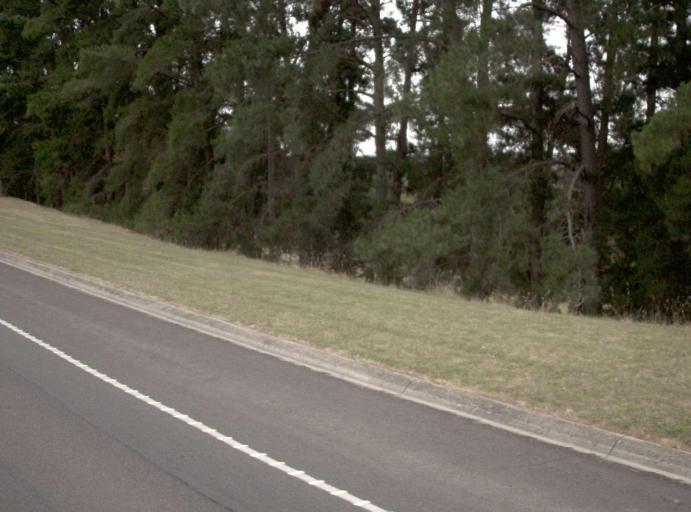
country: AU
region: Victoria
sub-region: Yarra Ranges
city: Yarra Glen
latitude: -37.5887
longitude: 145.4125
